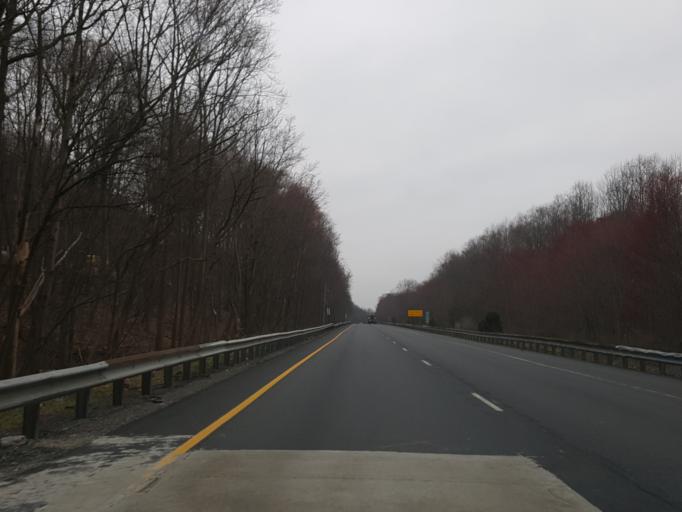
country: US
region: Pennsylvania
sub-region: Schuylkill County
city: Pine Grove
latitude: 40.5216
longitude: -76.4517
